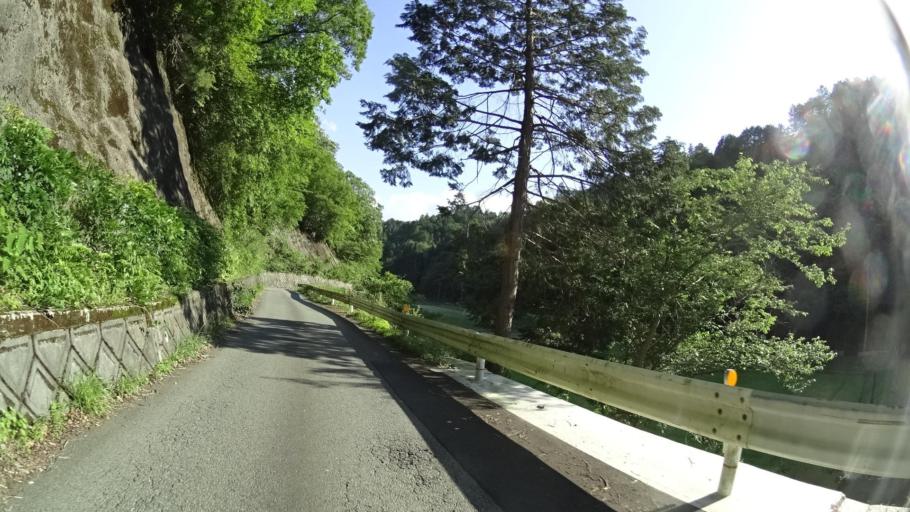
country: JP
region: Kyoto
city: Kameoka
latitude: 34.9717
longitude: 135.5621
